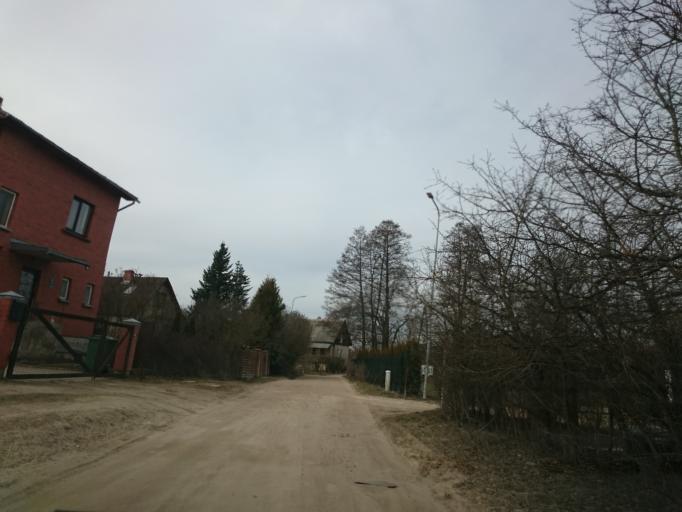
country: LV
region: Garkalne
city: Garkalne
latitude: 57.0150
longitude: 24.3935
